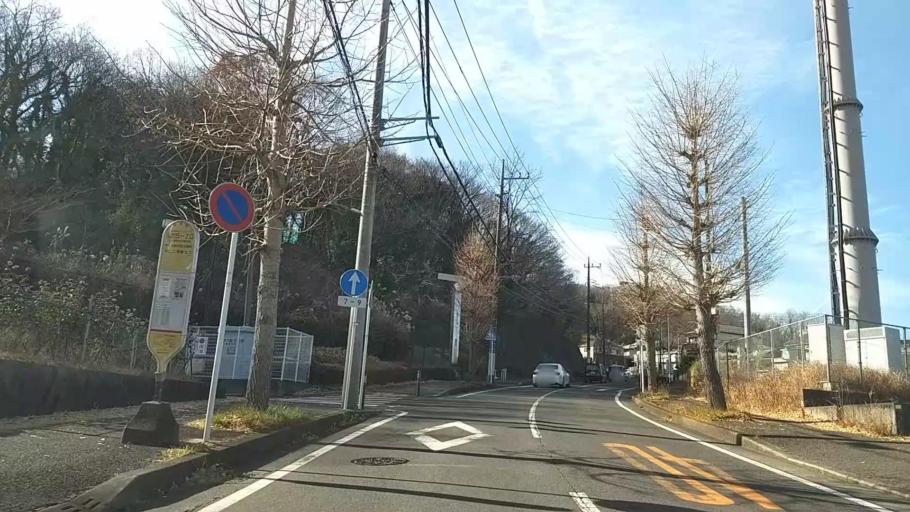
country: JP
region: Kanagawa
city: Hadano
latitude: 35.3599
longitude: 139.2259
